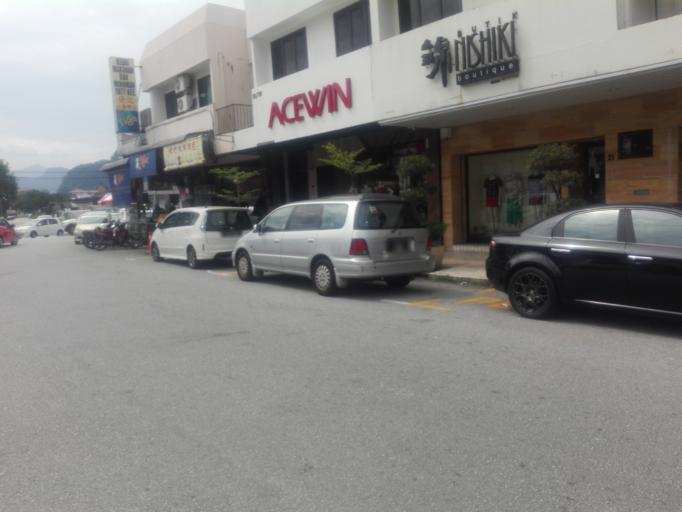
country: MY
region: Perak
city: Ipoh
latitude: 4.6067
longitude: 101.1197
